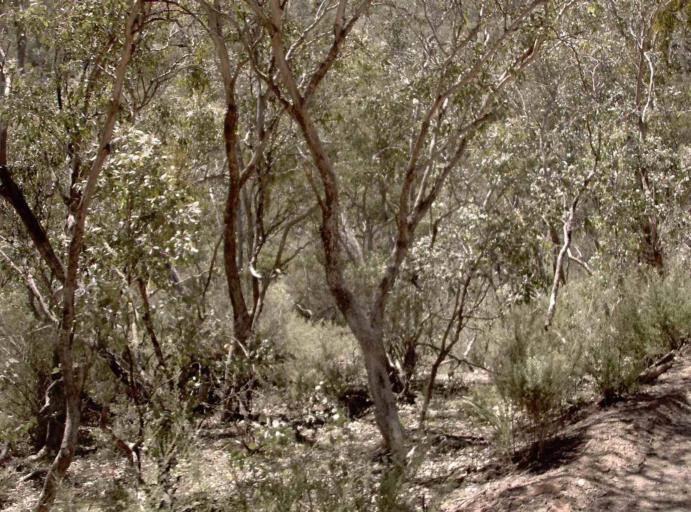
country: AU
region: New South Wales
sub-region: Snowy River
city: Jindabyne
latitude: -37.0631
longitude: 148.5170
